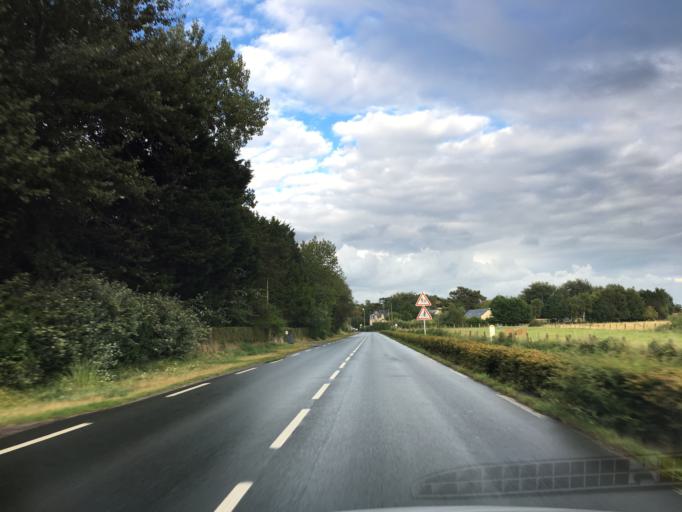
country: FR
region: Lower Normandy
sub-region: Departement du Calvados
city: Merville-Franceville-Plage
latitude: 49.2847
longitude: -0.1740
